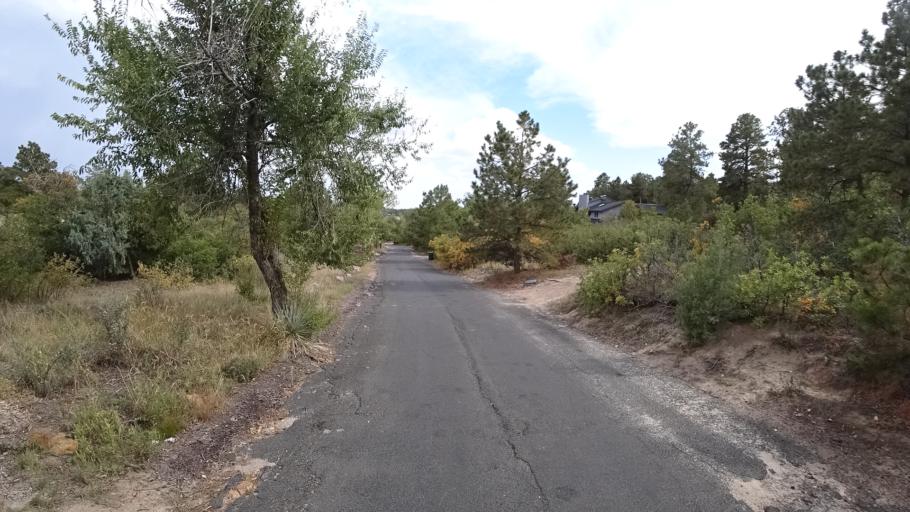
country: US
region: Colorado
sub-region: El Paso County
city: Cimarron Hills
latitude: 38.8753
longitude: -104.7614
